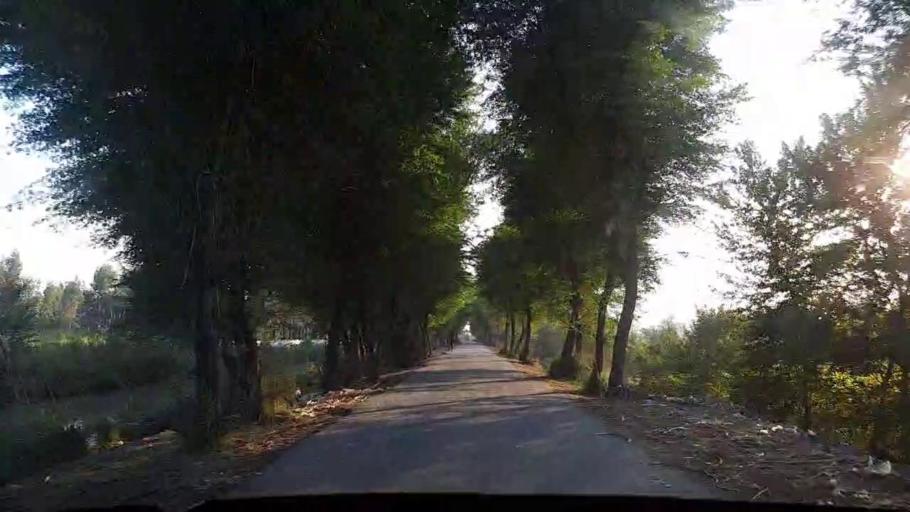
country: PK
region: Sindh
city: Sobhadero
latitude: 27.3904
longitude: 68.3841
